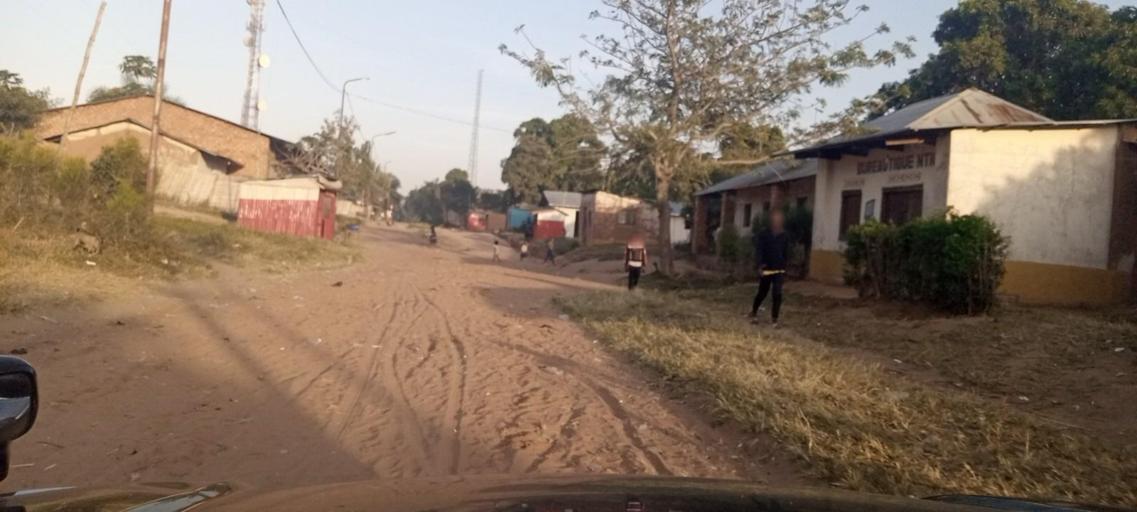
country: CD
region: Kasai-Oriental
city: Lubao
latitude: -5.3845
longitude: 25.7481
